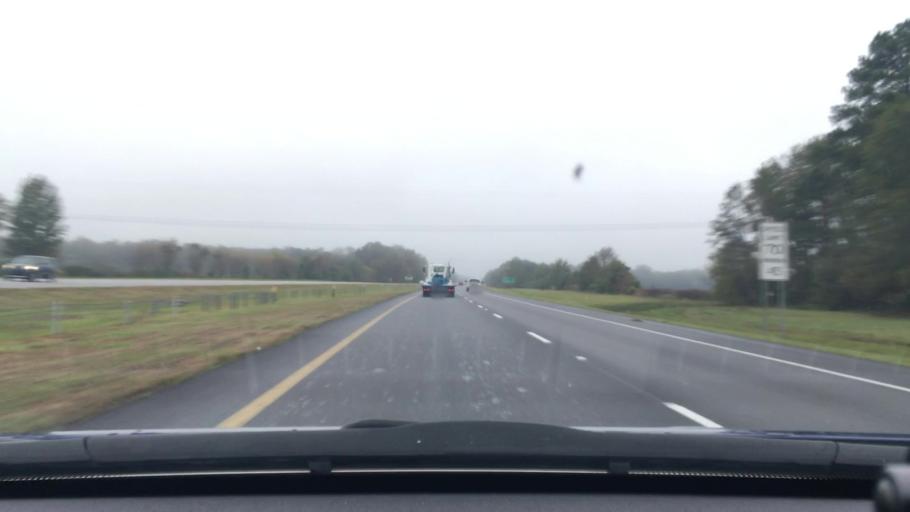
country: US
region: South Carolina
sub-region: Lee County
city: Bishopville
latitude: 34.1865
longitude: -80.2247
